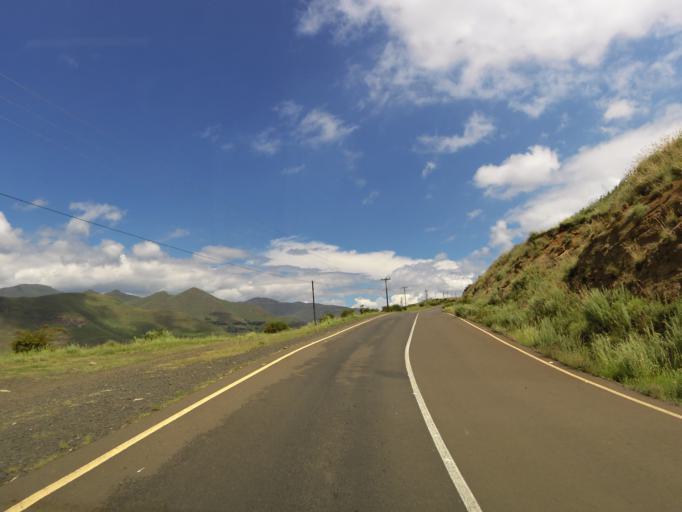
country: LS
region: Thaba-Tseka
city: Thaba-Tseka
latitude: -29.1343
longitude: 28.4937
